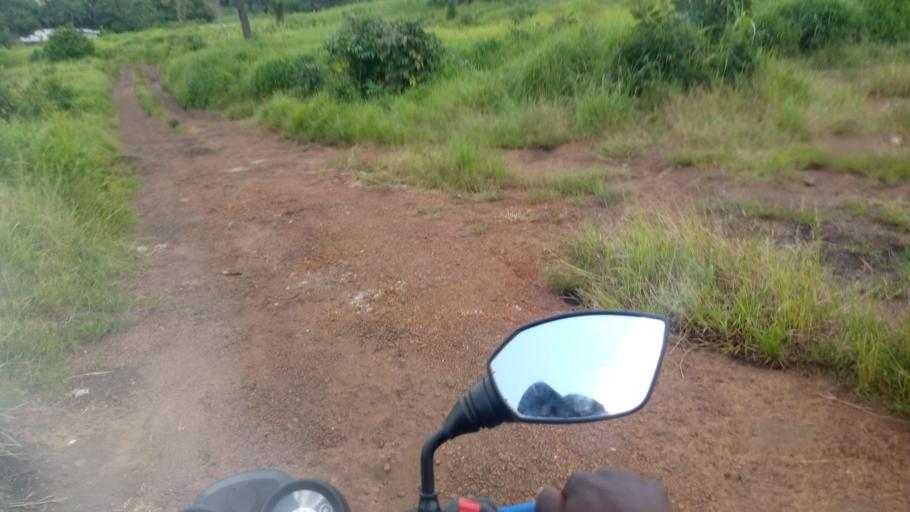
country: SL
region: Northern Province
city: Kamakwie
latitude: 9.4904
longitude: -12.2338
